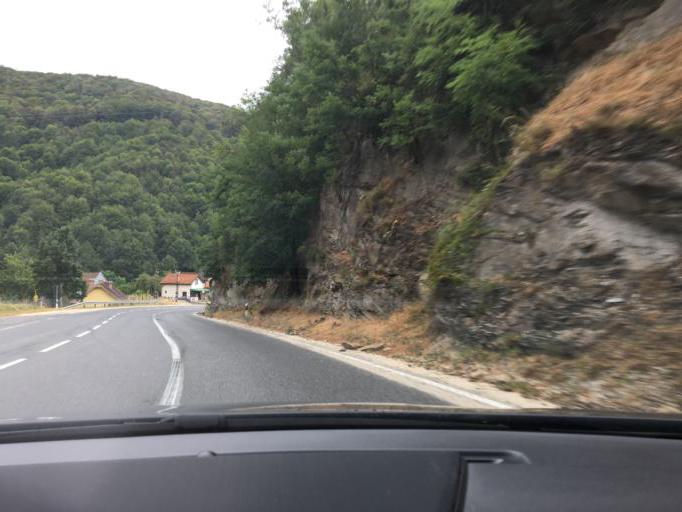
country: MK
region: Kriva Palanka
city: Kriva Palanka
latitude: 42.2236
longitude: 22.4257
